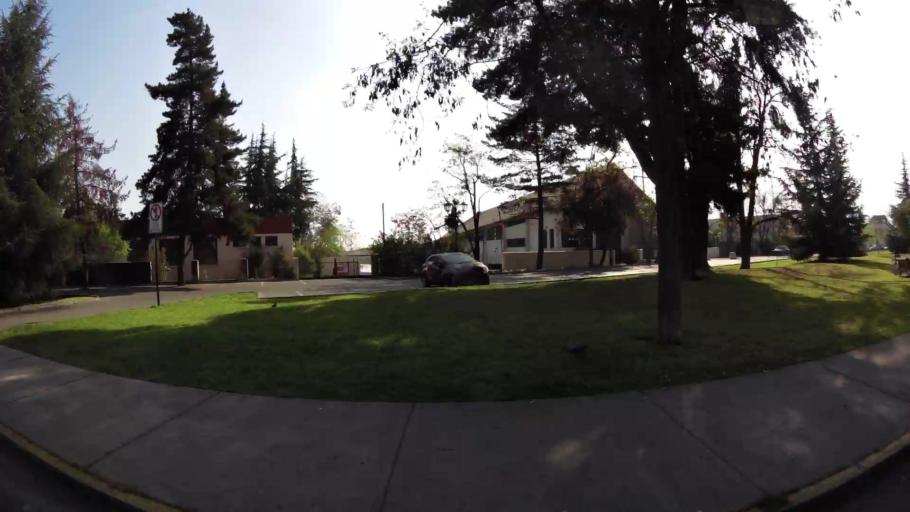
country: CL
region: Santiago Metropolitan
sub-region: Provincia de Santiago
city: Villa Presidente Frei, Nunoa, Santiago, Chile
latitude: -33.3899
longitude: -70.5532
